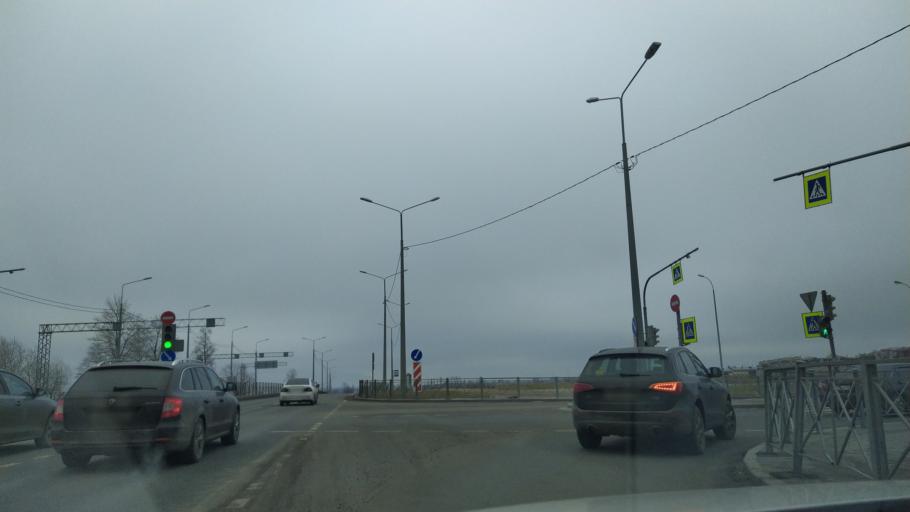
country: RU
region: St.-Petersburg
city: Aleksandrovskaya
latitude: 59.7600
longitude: 30.3700
